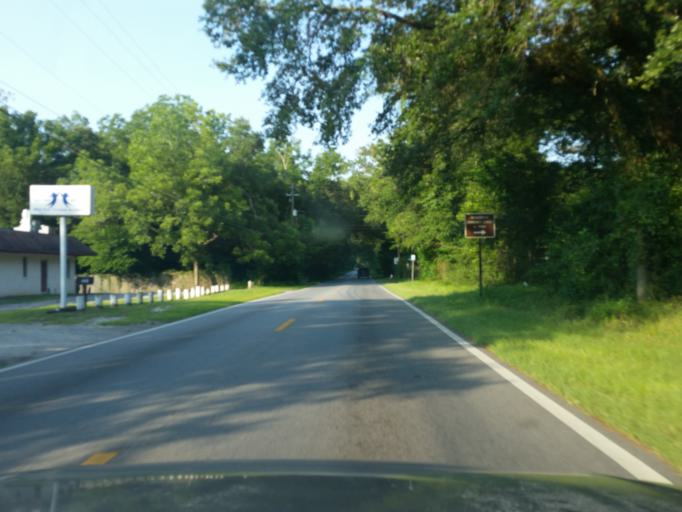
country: US
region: Florida
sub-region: Escambia County
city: Ensley
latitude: 30.4950
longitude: -87.2733
